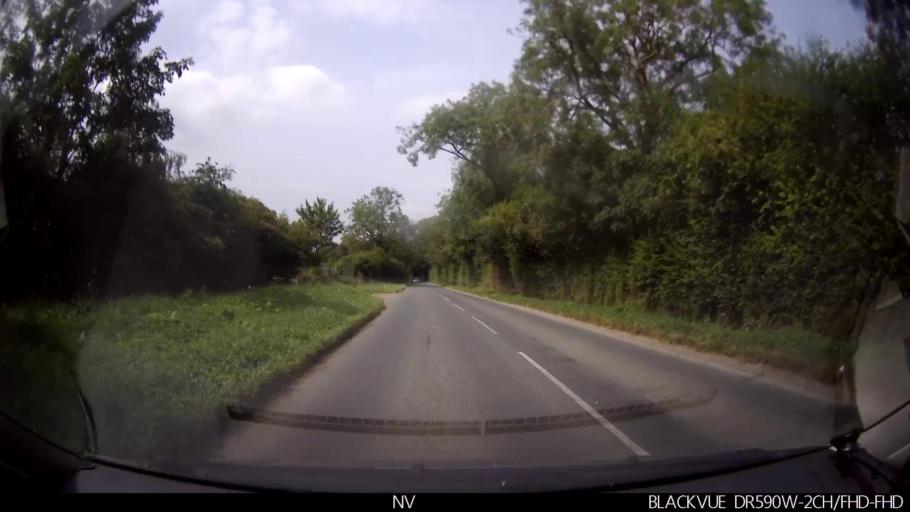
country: GB
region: England
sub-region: North Yorkshire
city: Marishes
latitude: 54.2063
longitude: -0.7992
